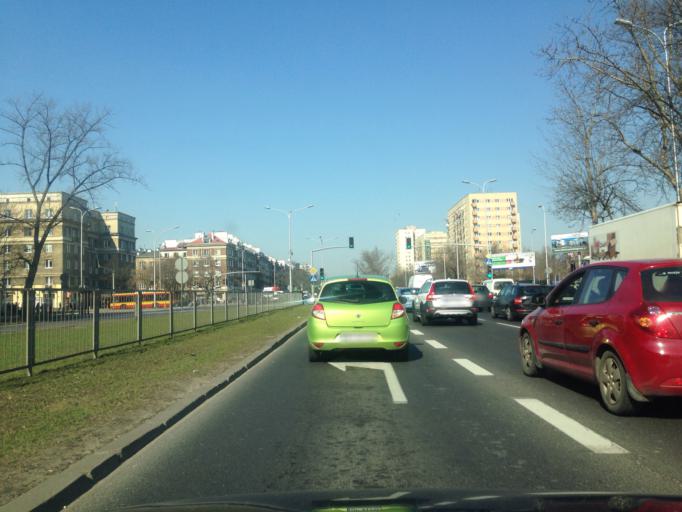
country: PL
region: Masovian Voivodeship
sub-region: Warszawa
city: Mokotow
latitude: 52.2063
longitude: 21.0488
